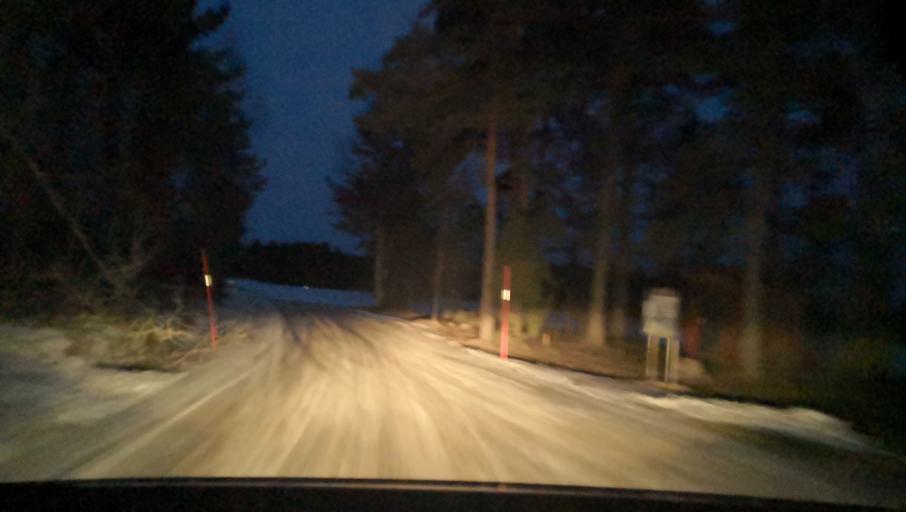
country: SE
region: Uppsala
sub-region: Heby Kommun
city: Tarnsjo
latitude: 60.2626
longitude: 16.7928
